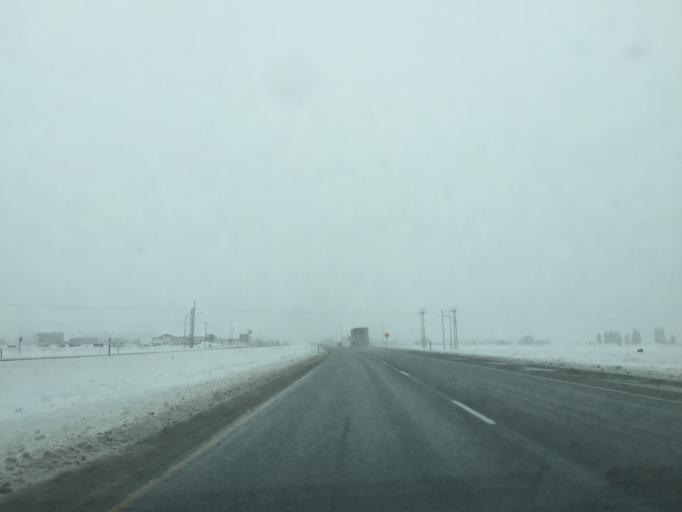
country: US
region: Washington
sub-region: Spokane County
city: Airway Heights
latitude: 47.5917
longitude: -117.5656
